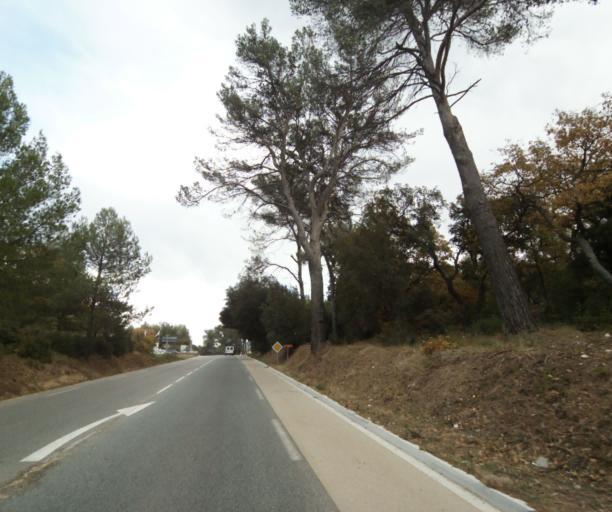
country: FR
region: Provence-Alpes-Cote d'Azur
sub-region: Departement des Bouches-du-Rhone
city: Cuges-les-Pins
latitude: 43.2659
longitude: 5.6686
